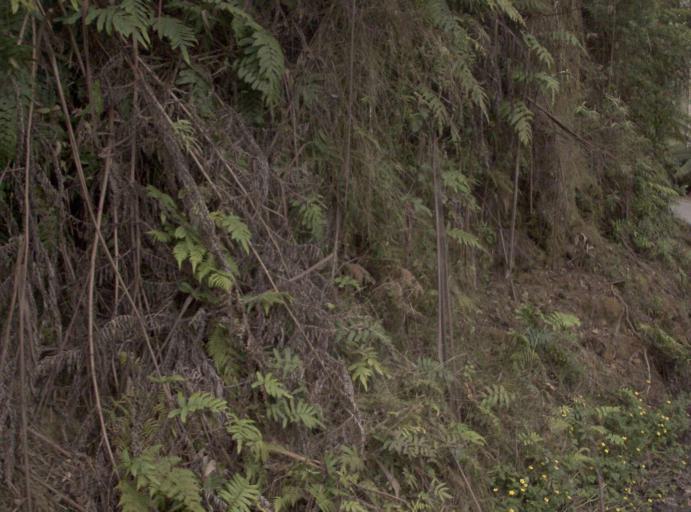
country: AU
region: Victoria
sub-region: Latrobe
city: Traralgon
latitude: -38.4252
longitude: 146.5686
